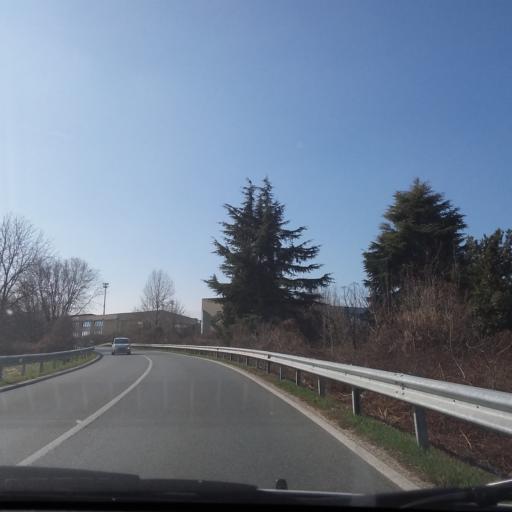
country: IT
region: Piedmont
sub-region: Provincia di Torino
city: Rivoli
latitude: 45.0669
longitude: 7.5332
